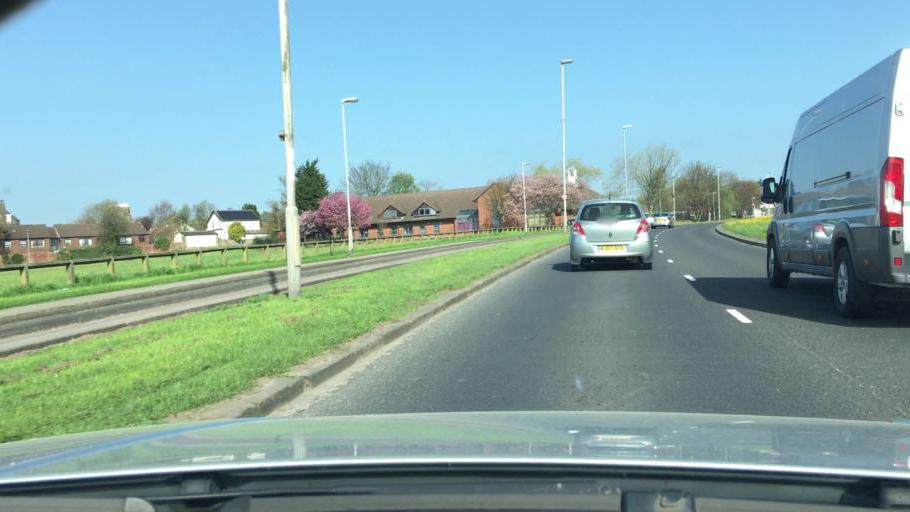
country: GB
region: England
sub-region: City and Borough of Leeds
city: Chapel Allerton
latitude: 53.8227
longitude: -1.5445
